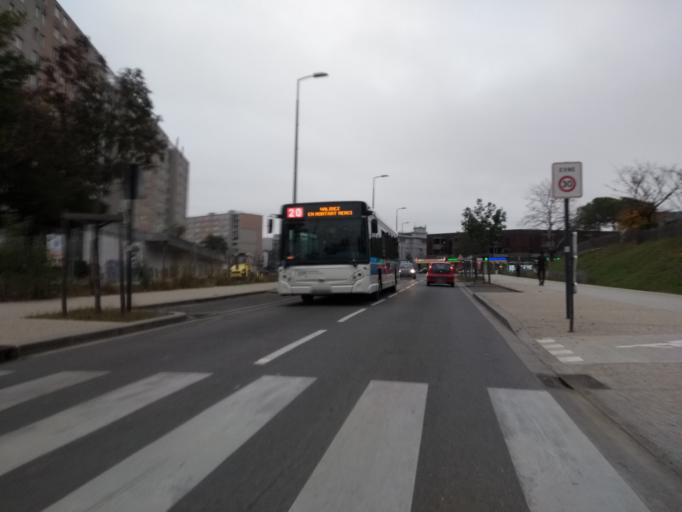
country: FR
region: Aquitaine
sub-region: Departement de la Gironde
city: Talence
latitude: 44.7899
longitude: -0.5872
